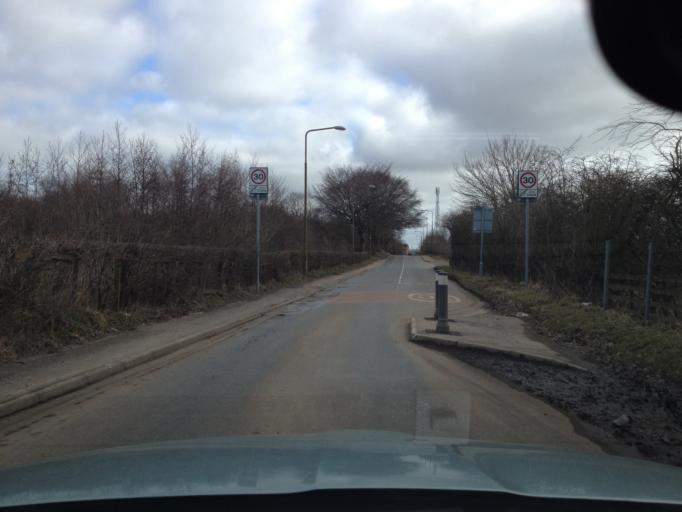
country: GB
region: Scotland
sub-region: West Lothian
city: Mid Calder
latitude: 55.9097
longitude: -3.4891
